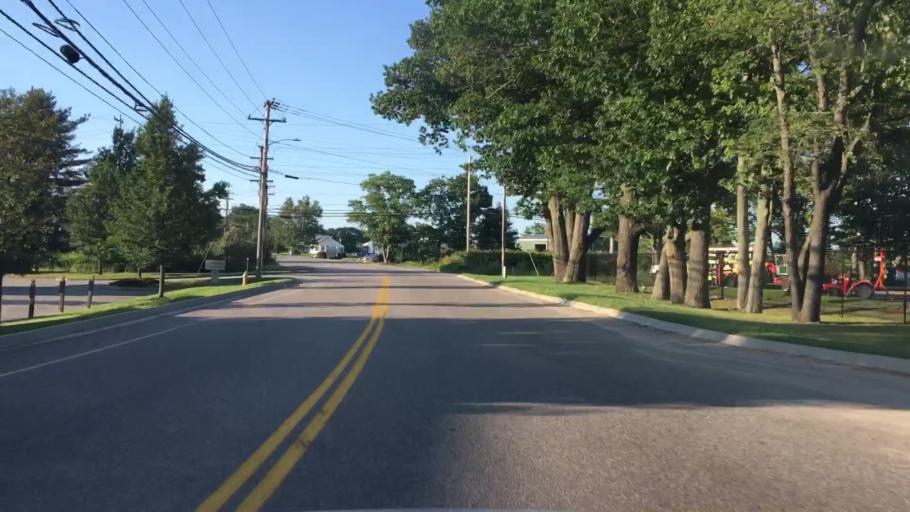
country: US
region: Maine
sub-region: Cumberland County
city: Scarborough
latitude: 43.5969
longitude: -70.2978
